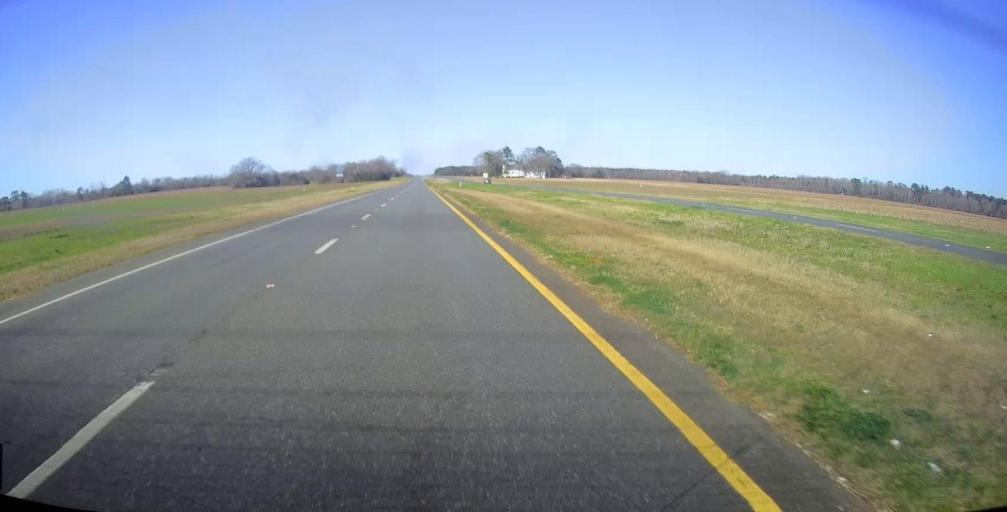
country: US
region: Georgia
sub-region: Schley County
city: Ellaville
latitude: 32.1684
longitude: -84.2693
